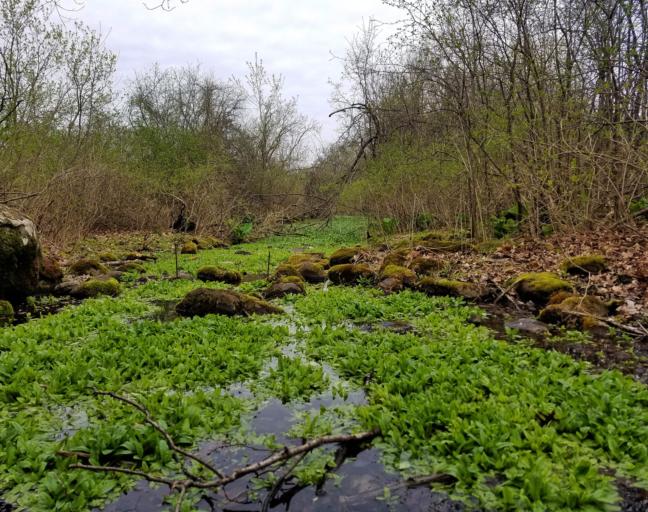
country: US
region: Wisconsin
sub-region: Dane County
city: Madison
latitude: 43.0479
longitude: -89.4252
